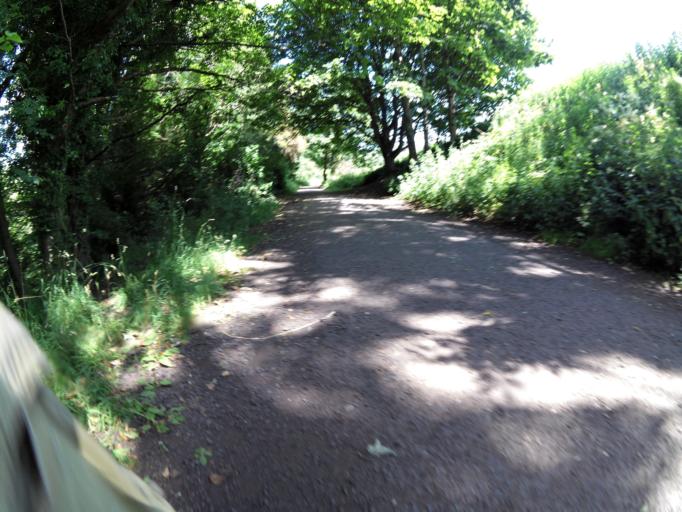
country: GB
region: Scotland
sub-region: Edinburgh
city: Currie
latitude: 55.8939
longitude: -3.3126
